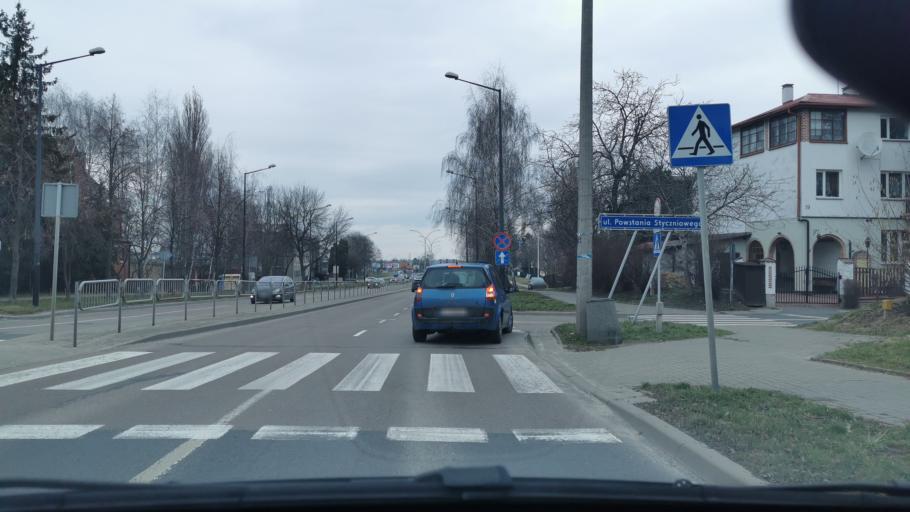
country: PL
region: Lublin Voivodeship
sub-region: Powiat lubelski
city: Lublin
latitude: 51.2440
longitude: 22.5064
